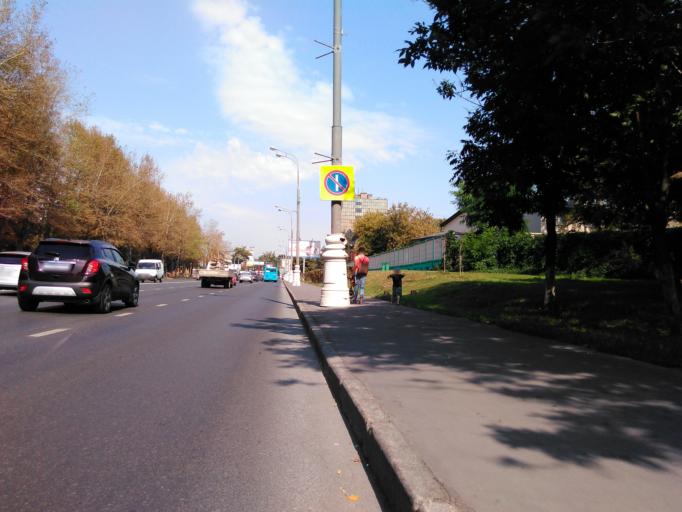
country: RU
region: Moscow
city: Novyye Cheremushki
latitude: 55.6979
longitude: 37.6129
